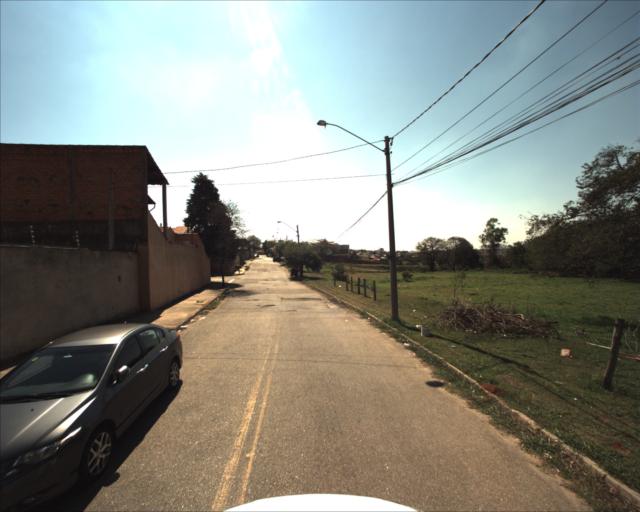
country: BR
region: Sao Paulo
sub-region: Sorocaba
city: Sorocaba
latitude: -23.5088
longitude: -47.5103
